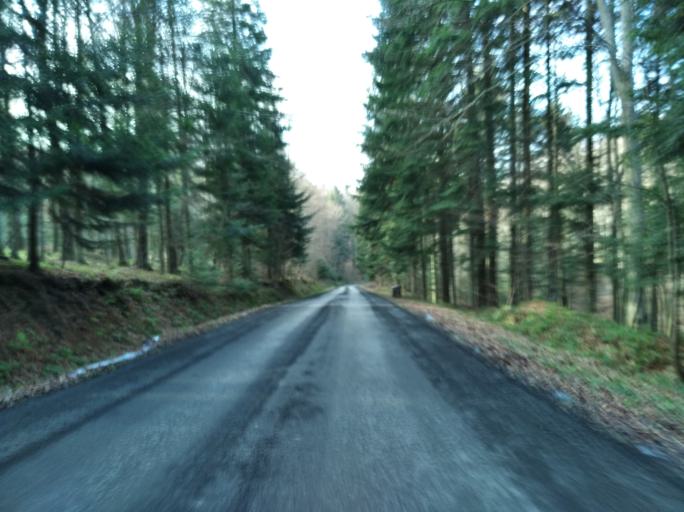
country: PL
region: Subcarpathian Voivodeship
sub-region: Powiat strzyzowski
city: Konieczkowa
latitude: 49.8247
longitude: 21.9486
